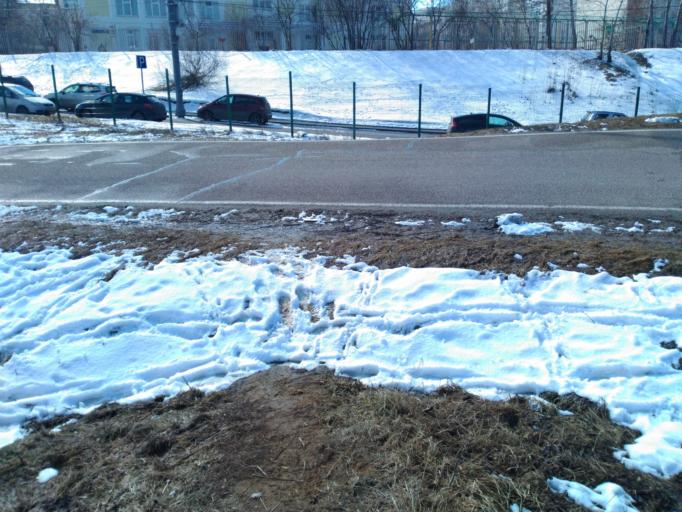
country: RU
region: Moscow
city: Shchukino
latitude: 55.7675
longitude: 37.4144
